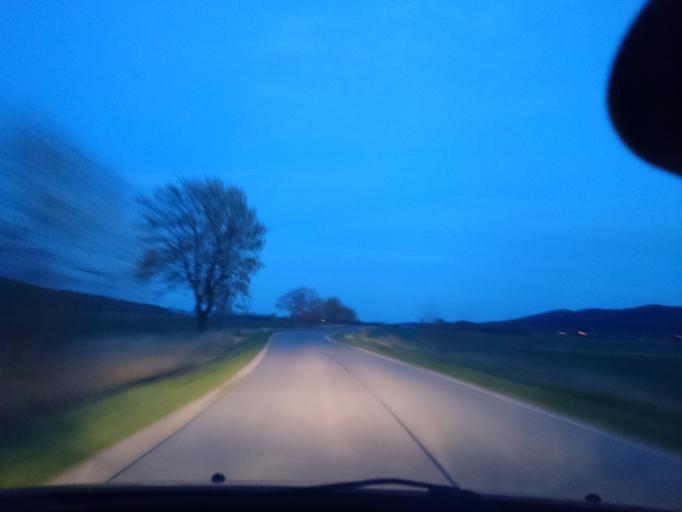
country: PL
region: Lower Silesian Voivodeship
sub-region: Powiat zabkowicki
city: Budzow
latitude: 50.5647
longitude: 16.6868
